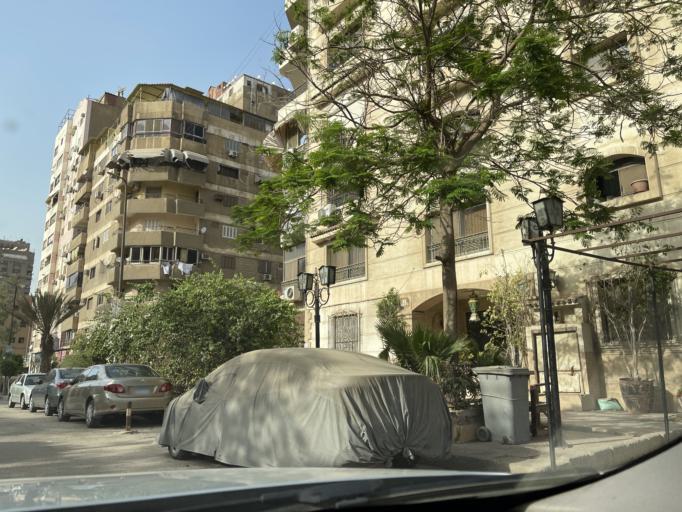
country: EG
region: Muhafazat al Qahirah
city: Cairo
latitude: 30.0663
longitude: 31.3530
